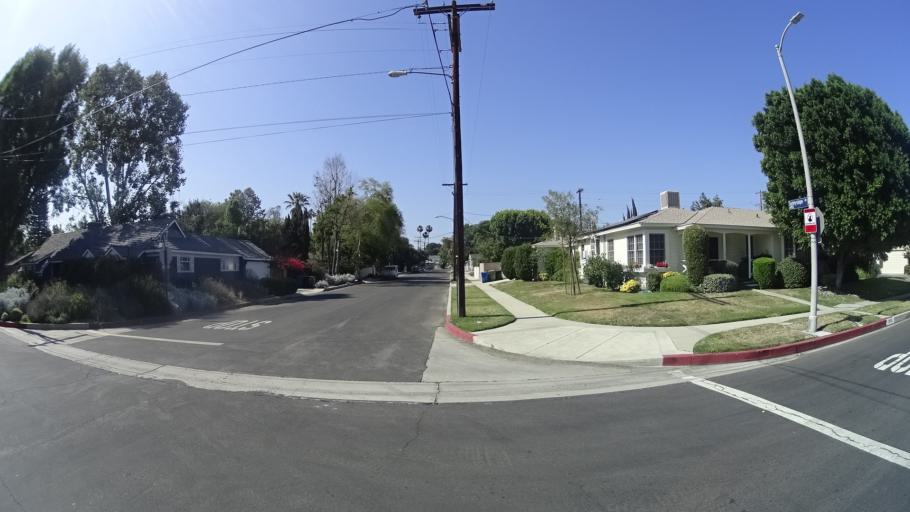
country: US
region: California
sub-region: Los Angeles County
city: Van Nuys
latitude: 34.1958
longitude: -118.4268
